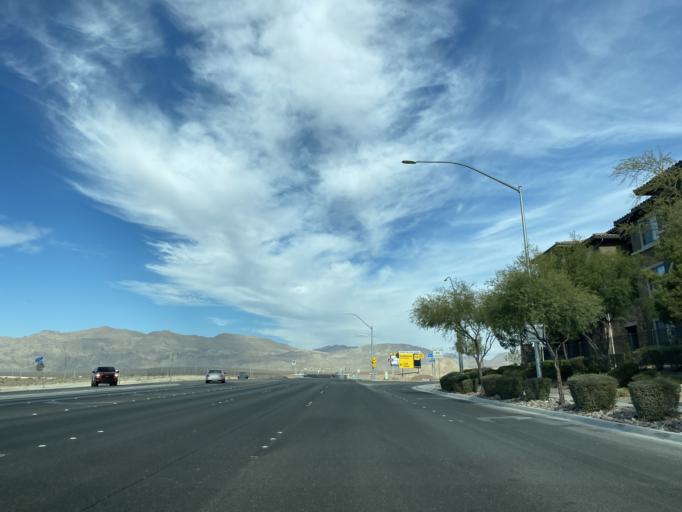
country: US
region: Nevada
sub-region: Clark County
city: Nellis Air Force Base
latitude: 36.2828
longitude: -115.1170
